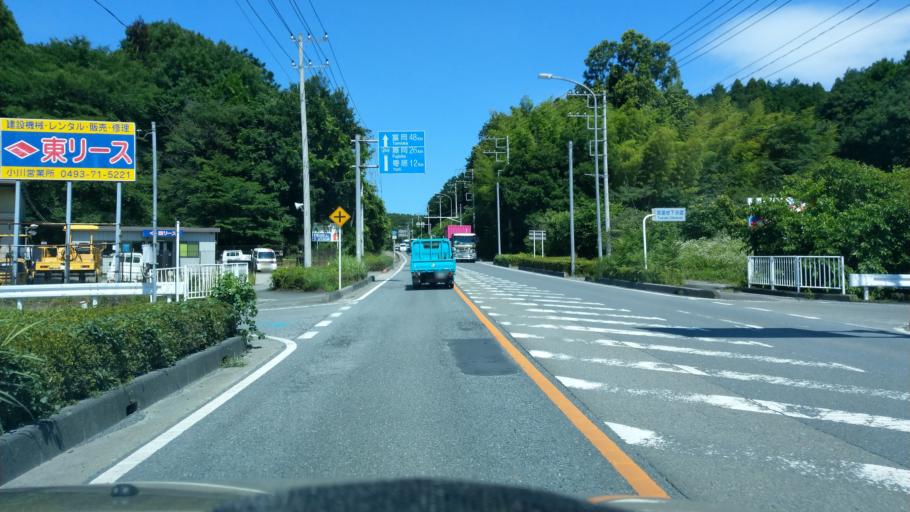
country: JP
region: Saitama
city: Ogawa
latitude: 36.0709
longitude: 139.2510
